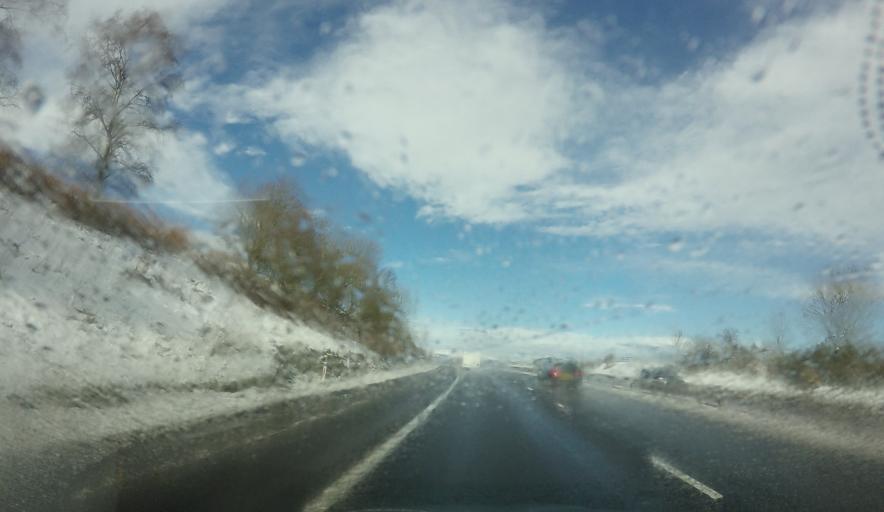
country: GB
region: Scotland
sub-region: Perth and Kinross
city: Perth
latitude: 56.3759
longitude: -3.4480
